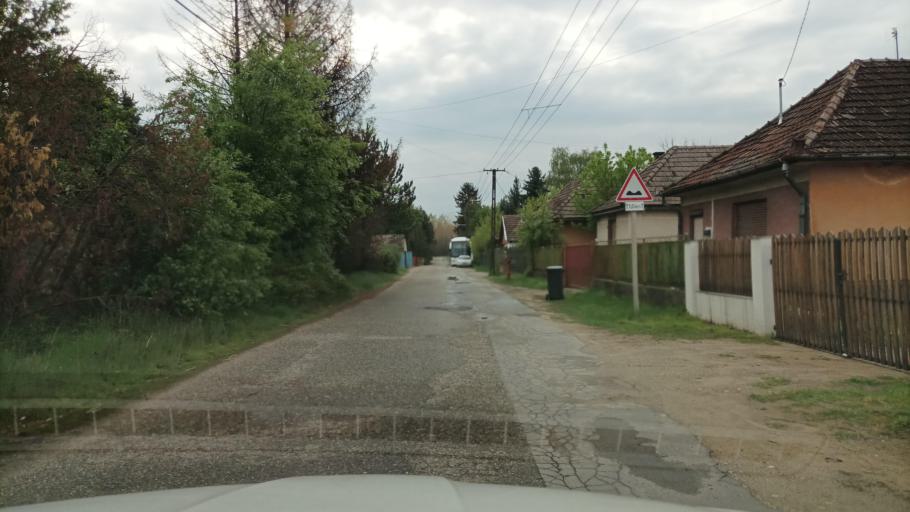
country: HU
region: Pest
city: Hernad
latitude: 47.1763
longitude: 19.4706
